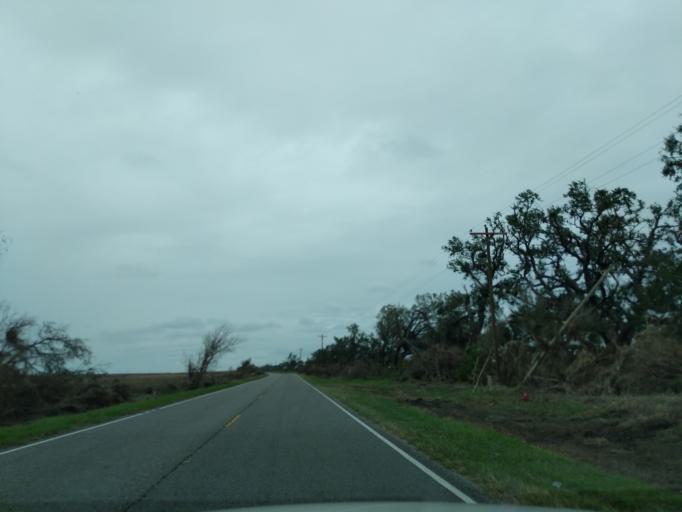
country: US
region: Louisiana
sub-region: Cameron Parish
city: Cameron
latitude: 29.7863
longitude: -93.1218
